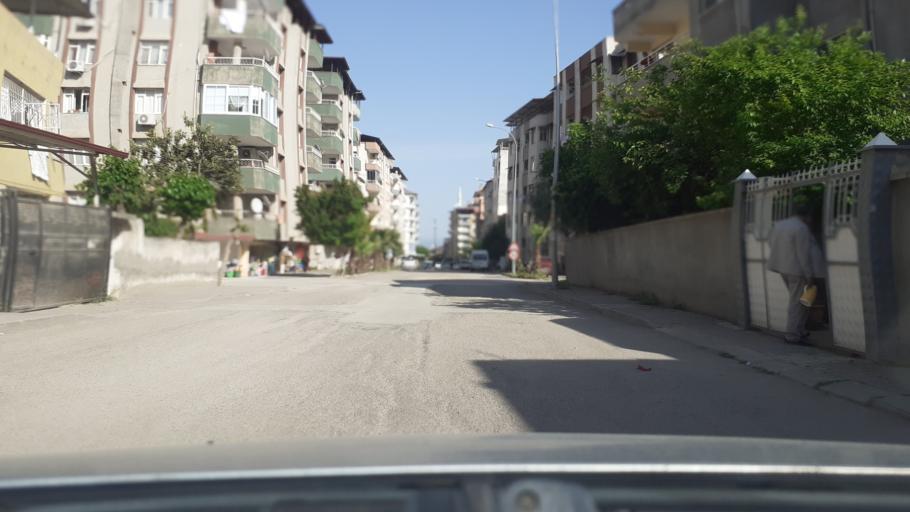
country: TR
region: Hatay
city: Kirikhan
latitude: 36.4963
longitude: 36.3654
